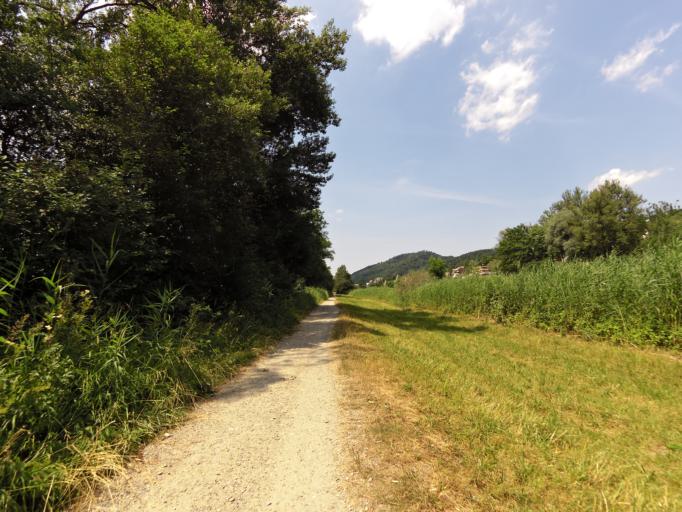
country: CH
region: Zurich
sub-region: Bezirk Dietikon
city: Geroldswil
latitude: 47.4236
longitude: 8.3991
